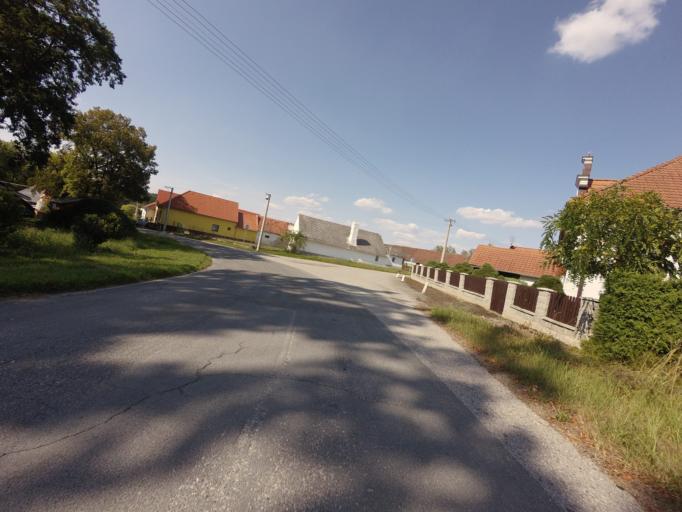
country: CZ
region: Jihocesky
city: Tyn nad Vltavou
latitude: 49.1489
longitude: 14.4450
